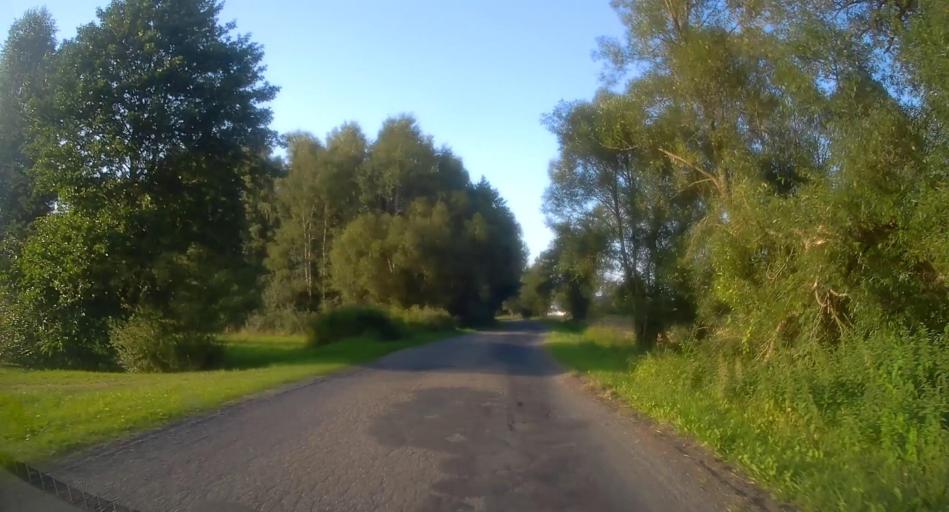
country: PL
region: Lodz Voivodeship
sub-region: Powiat skierniewicki
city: Kaweczyn Nowy
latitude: 51.8957
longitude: 20.2974
